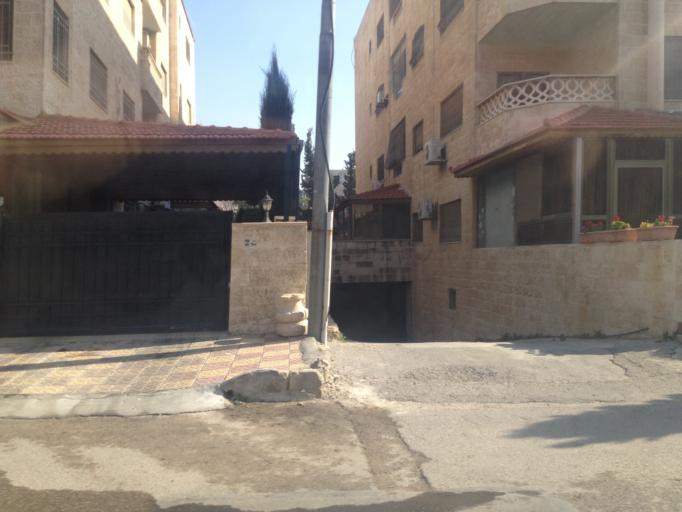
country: JO
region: Amman
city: Wadi as Sir
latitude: 31.9505
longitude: 35.8570
